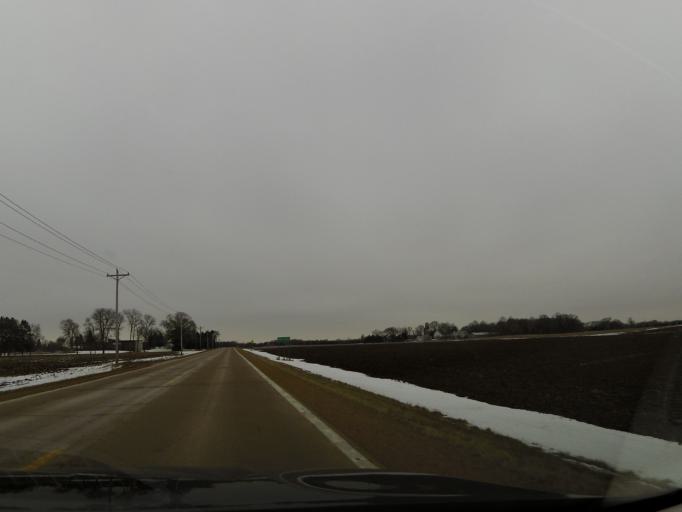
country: US
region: Minnesota
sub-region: Carver County
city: Carver
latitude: 44.7234
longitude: -93.6843
